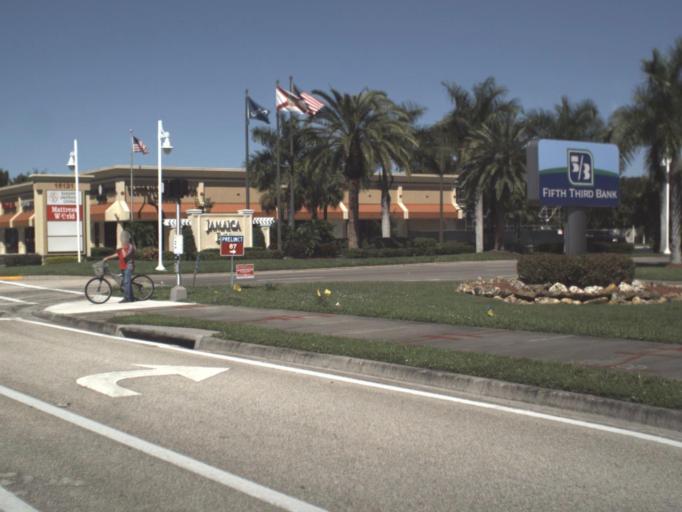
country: US
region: Florida
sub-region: Lee County
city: Villas
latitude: 26.5218
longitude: -81.8694
